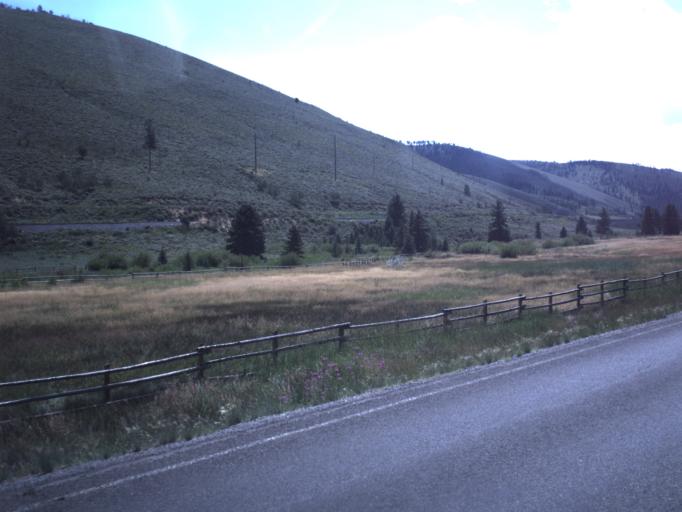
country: US
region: Utah
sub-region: Sanpete County
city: Fairview
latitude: 39.7115
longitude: -111.1633
